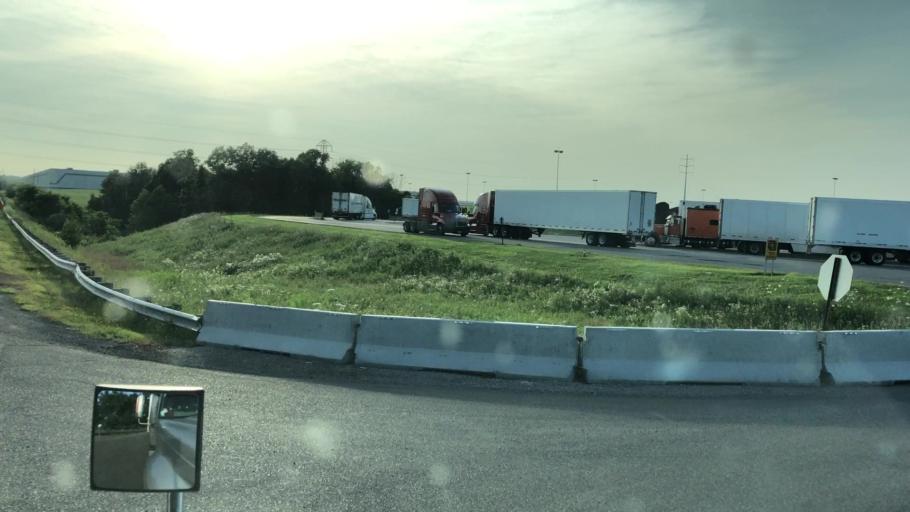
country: US
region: Ohio
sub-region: Muskingum County
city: Pleasant Grove
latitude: 39.9841
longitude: -81.9476
